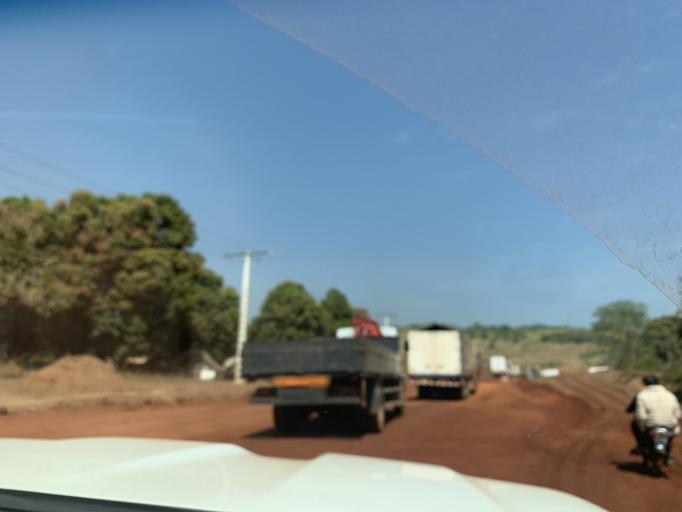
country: GN
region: Mamou
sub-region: Mamou Prefecture
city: Mamou
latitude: 10.2086
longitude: -12.4642
